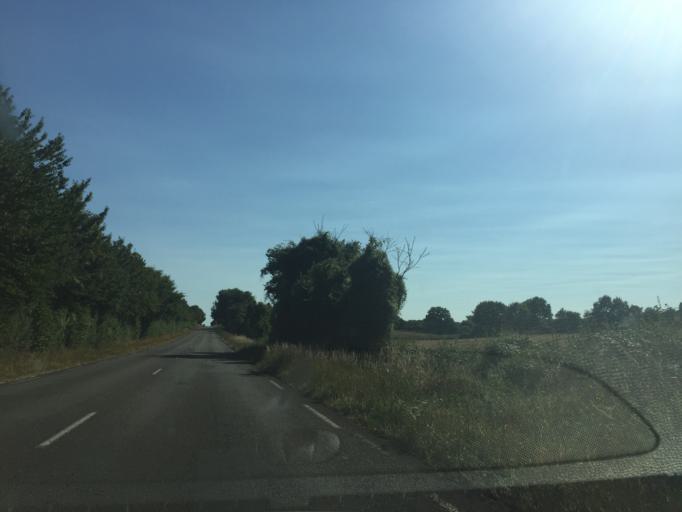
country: FR
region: Poitou-Charentes
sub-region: Departement des Deux-Sevres
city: Melle
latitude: 46.2502
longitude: -0.0995
